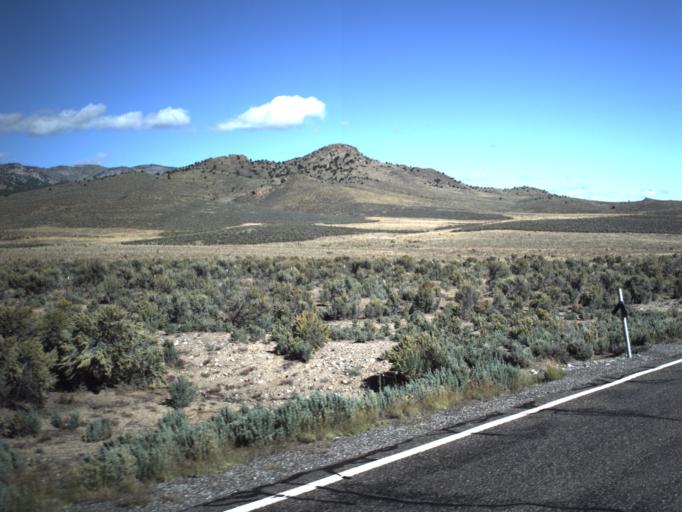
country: US
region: Utah
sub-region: Piute County
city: Junction
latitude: 38.2923
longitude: -111.9758
